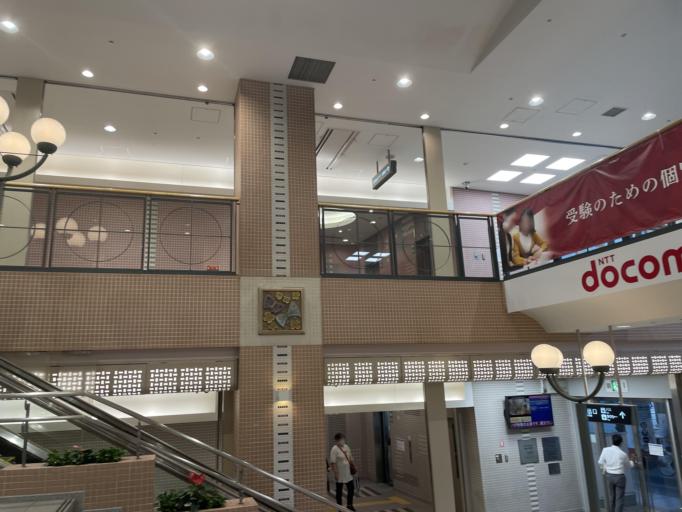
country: JP
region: Hyogo
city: Itami
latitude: 34.7804
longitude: 135.4131
